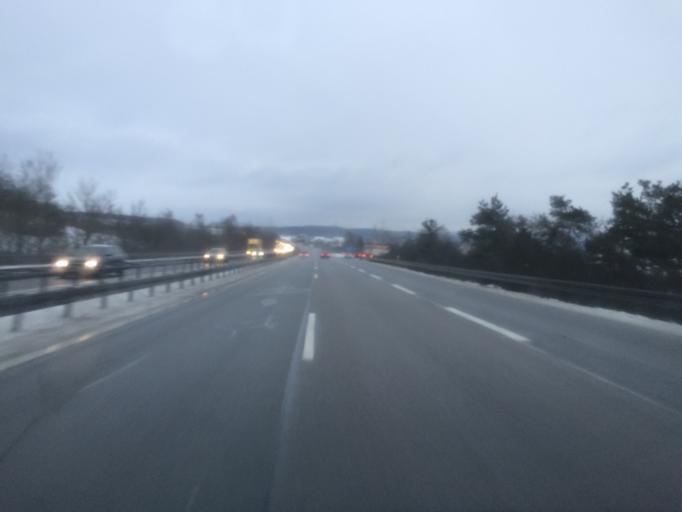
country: DE
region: Bavaria
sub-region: Upper Palatinate
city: Regenstauf
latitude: 49.1153
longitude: 12.1042
